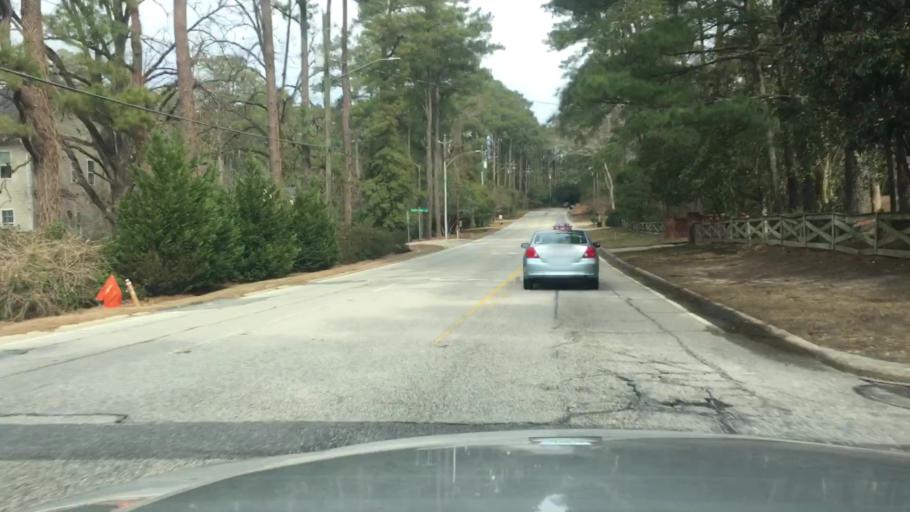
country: US
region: North Carolina
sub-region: Cumberland County
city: Fayetteville
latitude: 35.0508
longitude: -78.9137
